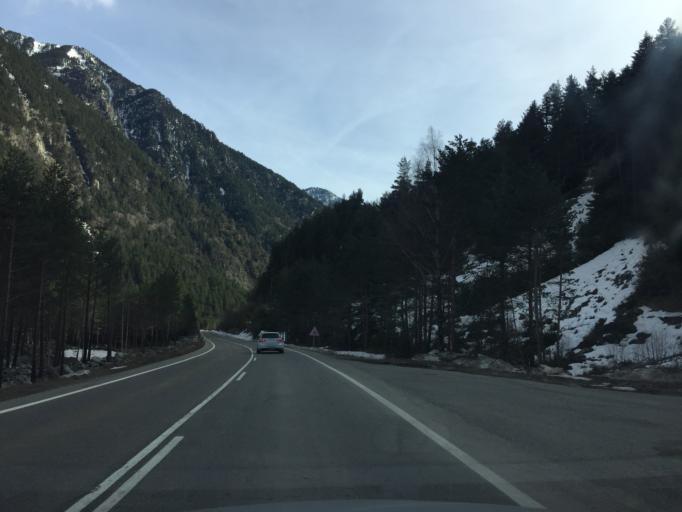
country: ES
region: Aragon
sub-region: Provincia de Huesca
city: Bielsa
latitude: 42.6888
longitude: 0.2081
